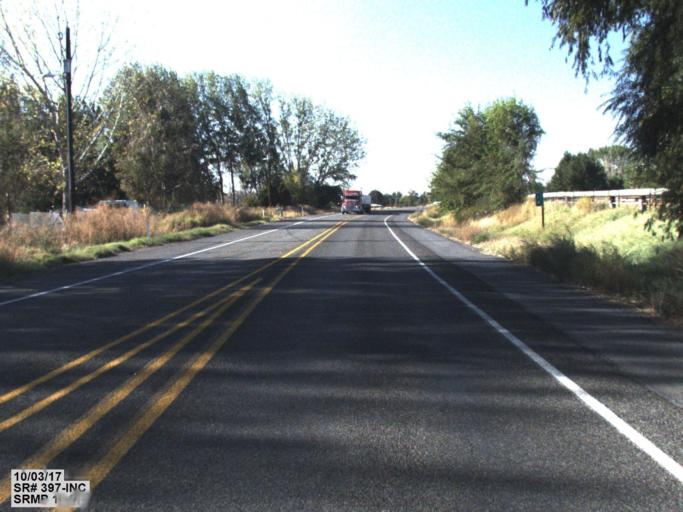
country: US
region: Washington
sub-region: Benton County
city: Finley
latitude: 46.1739
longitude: -119.0562
